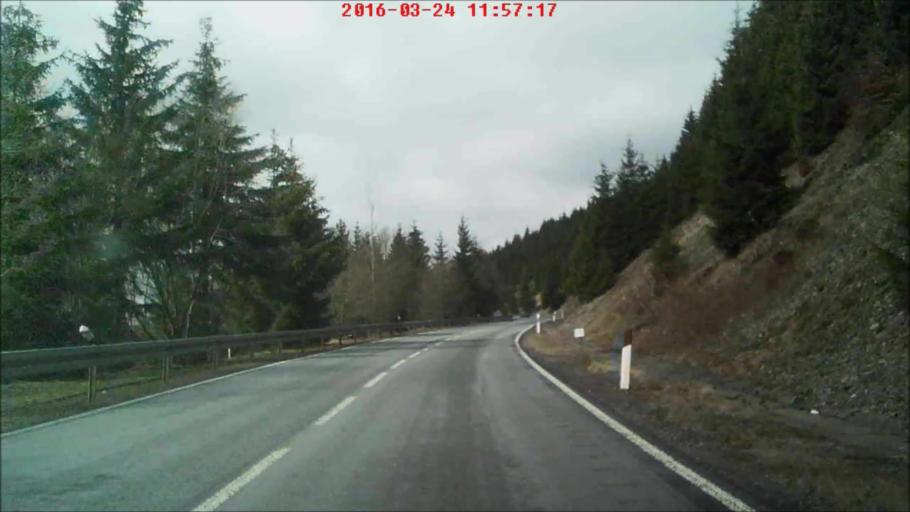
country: DE
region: Thuringia
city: Steinheid
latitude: 50.4933
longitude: 11.0572
